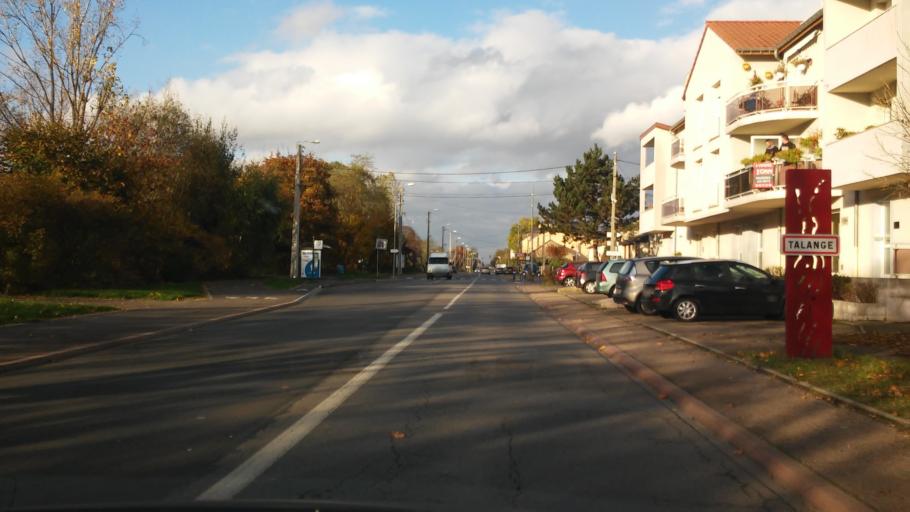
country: FR
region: Lorraine
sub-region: Departement de la Moselle
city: Talange
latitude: 49.2268
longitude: 6.1670
